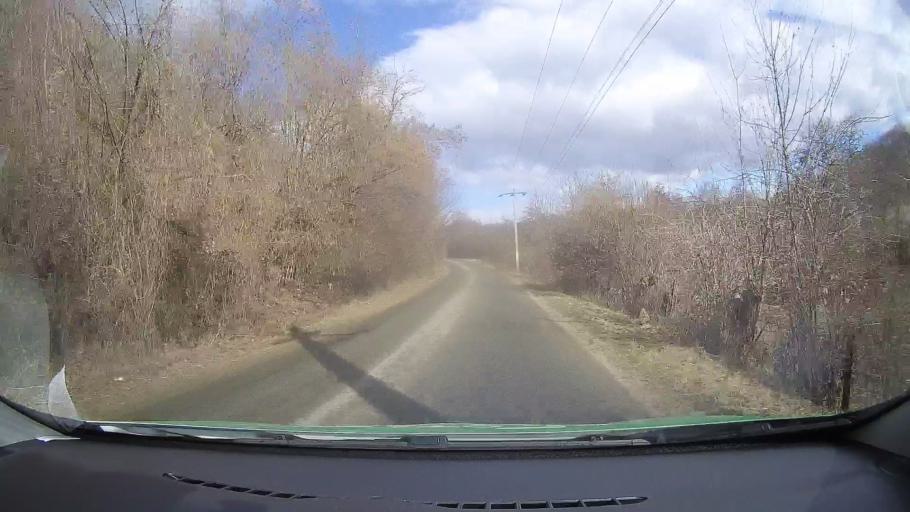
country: RO
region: Dambovita
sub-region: Comuna Motaeni
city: Motaeni
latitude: 45.1070
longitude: 25.4423
